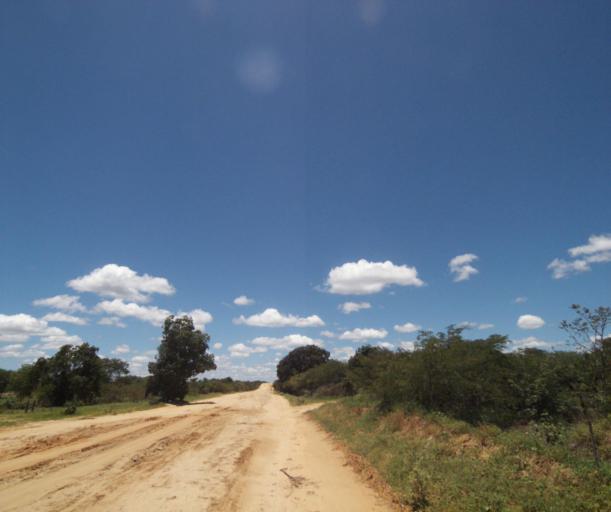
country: BR
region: Bahia
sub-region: Carinhanha
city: Carinhanha
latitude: -14.2833
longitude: -43.7895
